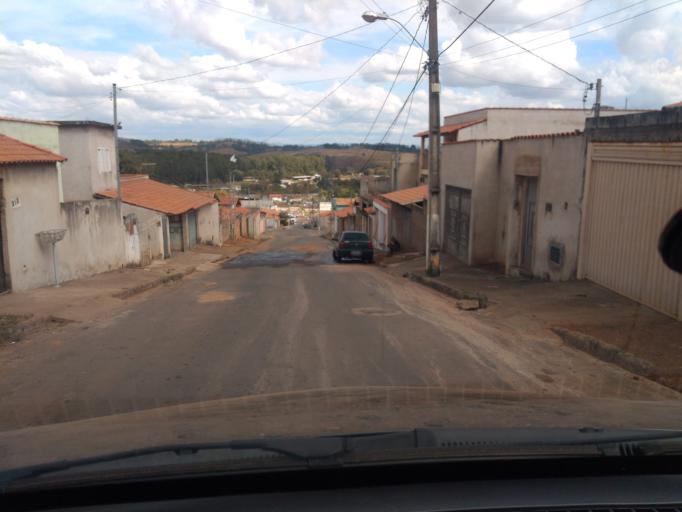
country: BR
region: Minas Gerais
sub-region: Tres Coracoes
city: Tres Coracoes
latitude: -21.6952
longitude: -45.2406
